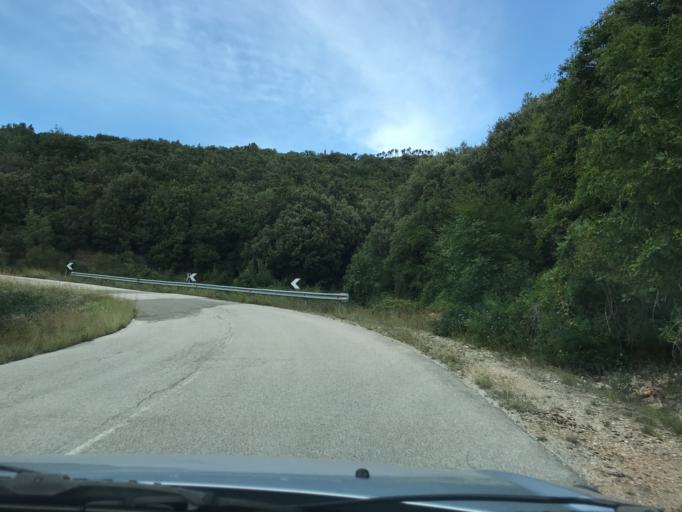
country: IT
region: Umbria
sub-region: Provincia di Terni
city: Montecchio
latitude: 42.6863
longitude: 12.2977
